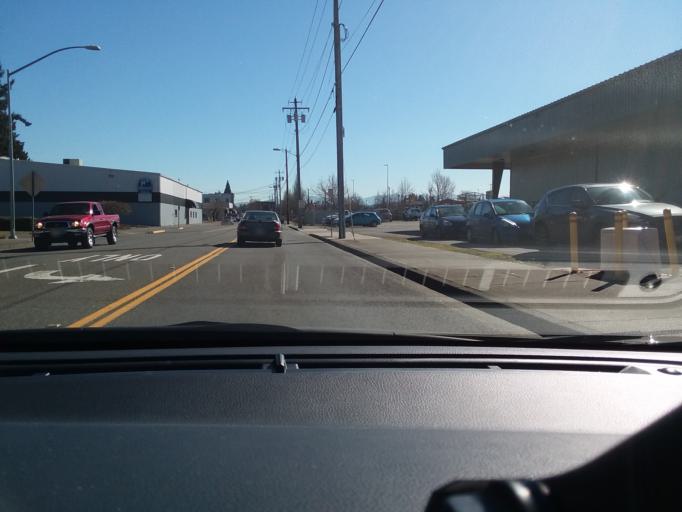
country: US
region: Washington
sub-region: Pierce County
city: Puyallup
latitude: 47.1936
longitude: -122.2982
